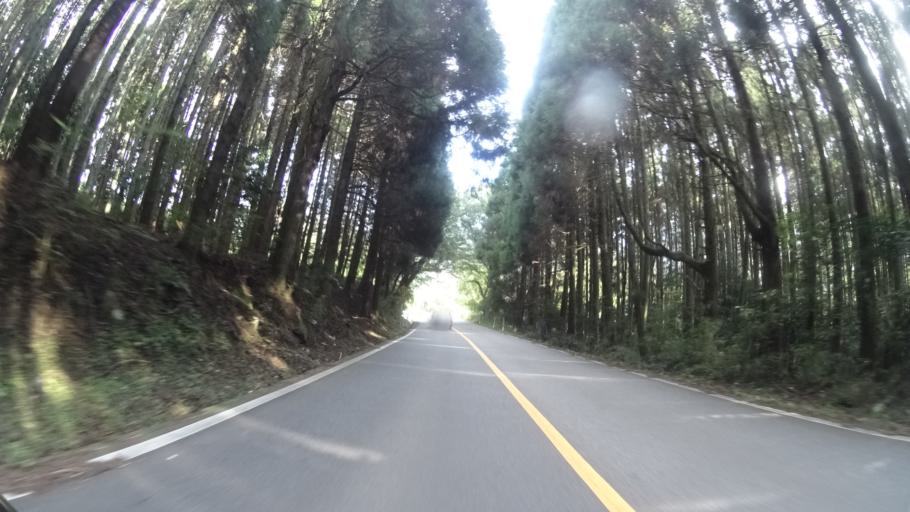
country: JP
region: Oita
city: Beppu
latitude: 33.2630
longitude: 131.3751
